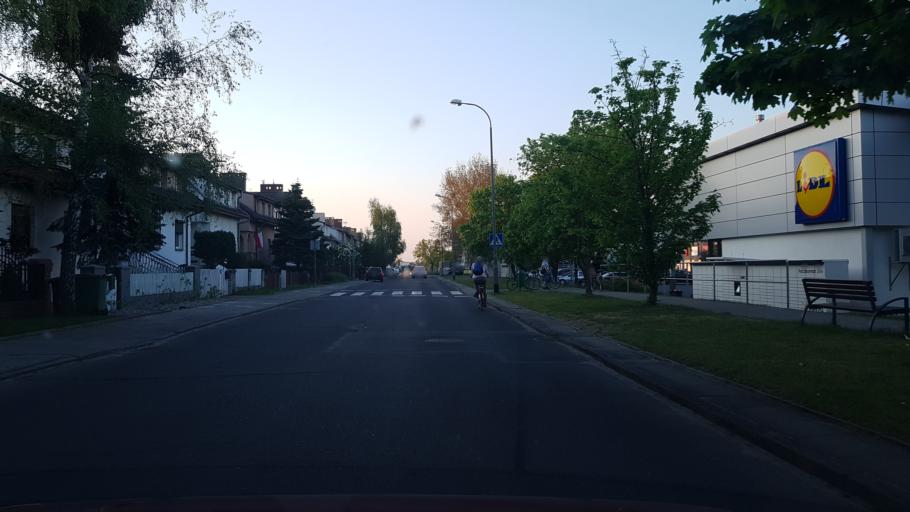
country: PL
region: West Pomeranian Voivodeship
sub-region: Szczecin
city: Szczecin
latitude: 53.3781
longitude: 14.6682
